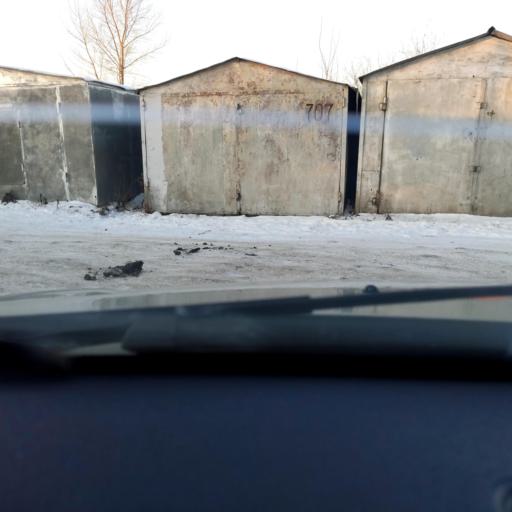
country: RU
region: Bashkortostan
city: Mikhaylovka
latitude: 54.7167
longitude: 55.8284
